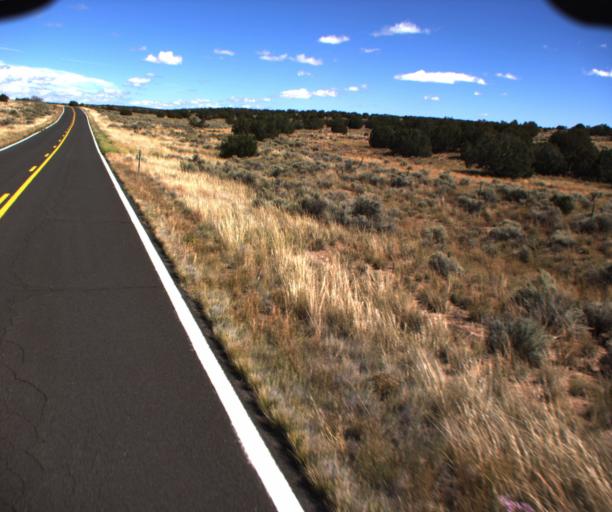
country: US
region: Arizona
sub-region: Apache County
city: Houck
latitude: 34.9408
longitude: -109.1795
